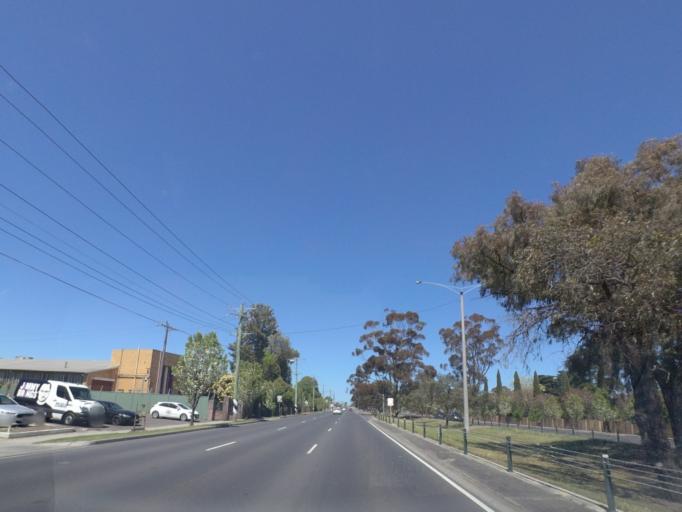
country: AU
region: Victoria
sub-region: Moreland
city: Fawkner
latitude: -37.7118
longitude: 144.9618
